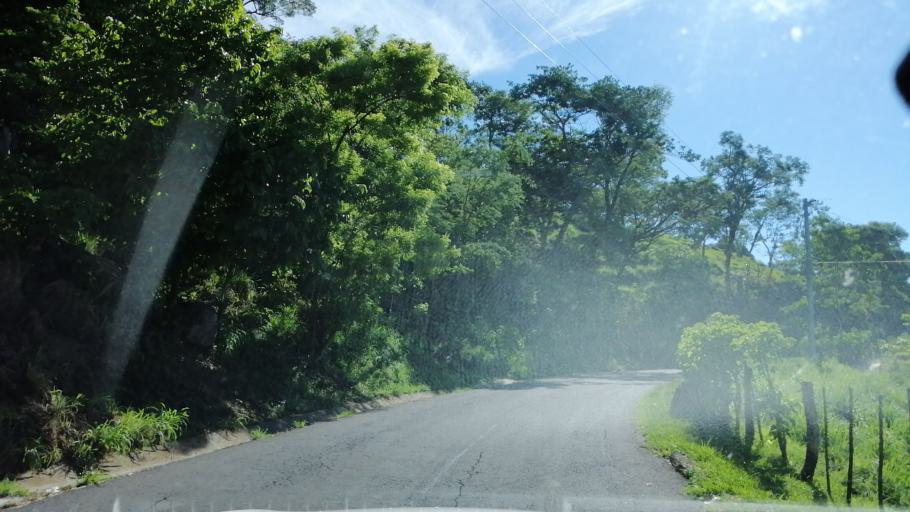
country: SV
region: Morazan
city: Corinto
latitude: 13.7989
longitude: -88.0042
